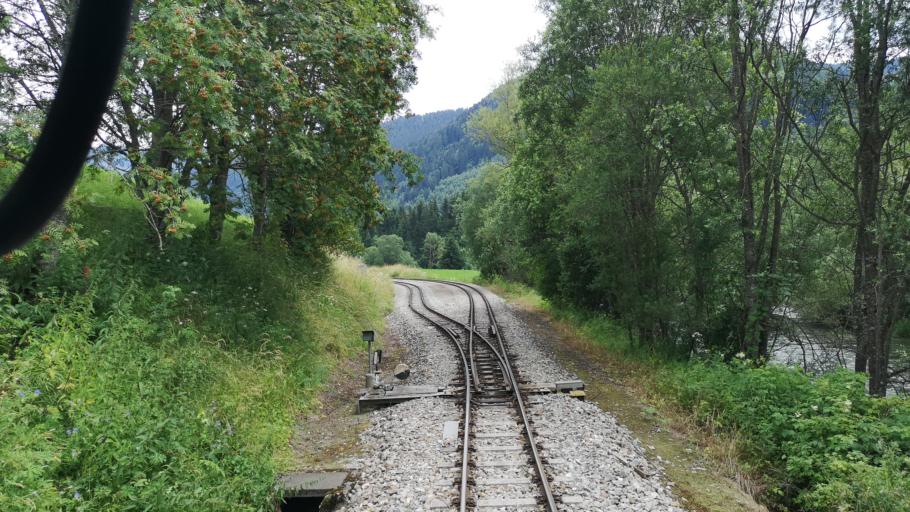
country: AT
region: Salzburg
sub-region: Politischer Bezirk Tamsweg
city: Ramingstein
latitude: 47.0703
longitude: 13.8781
